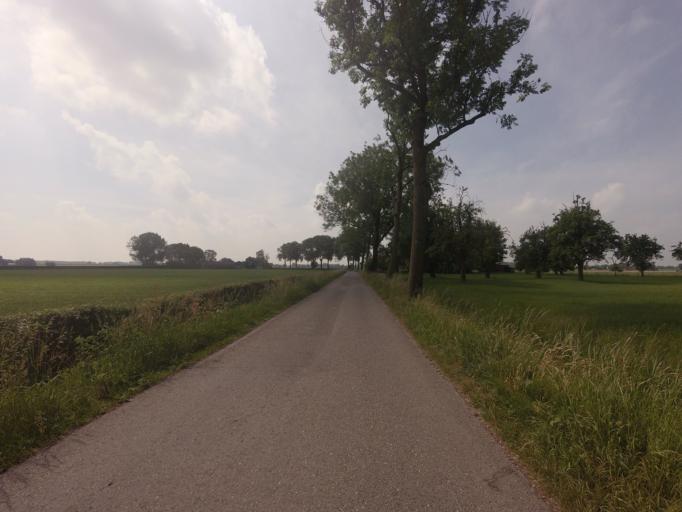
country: NL
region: Utrecht
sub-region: Gemeente IJsselstein
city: IJsselstein
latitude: 52.0052
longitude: 5.0598
